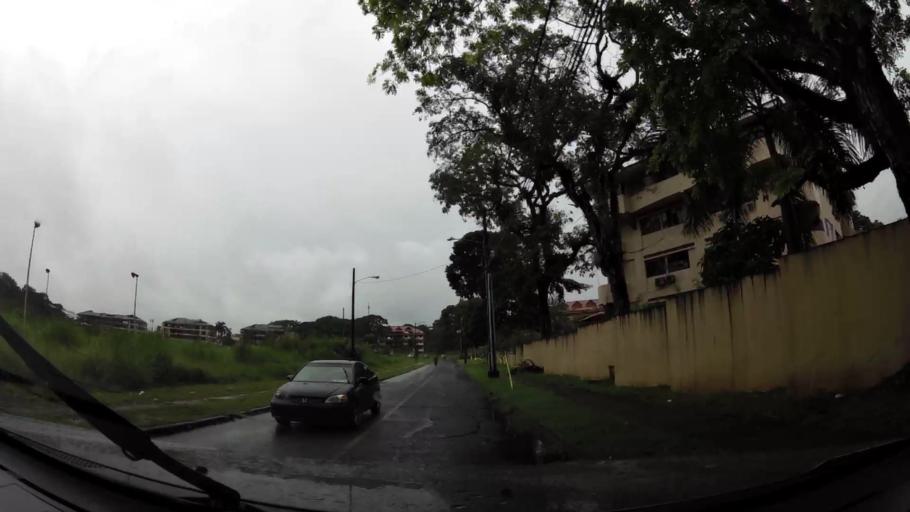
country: PA
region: Colon
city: Las Margaritas
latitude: 9.3159
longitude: -79.8773
